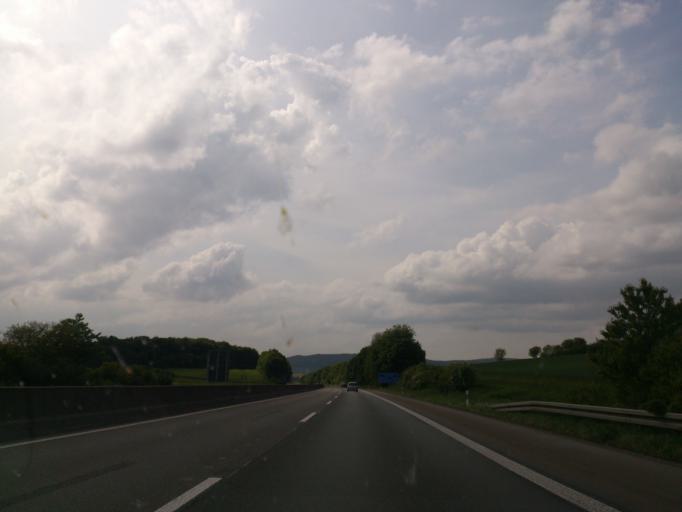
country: DE
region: North Rhine-Westphalia
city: Warburg
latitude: 51.4730
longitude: 9.0983
